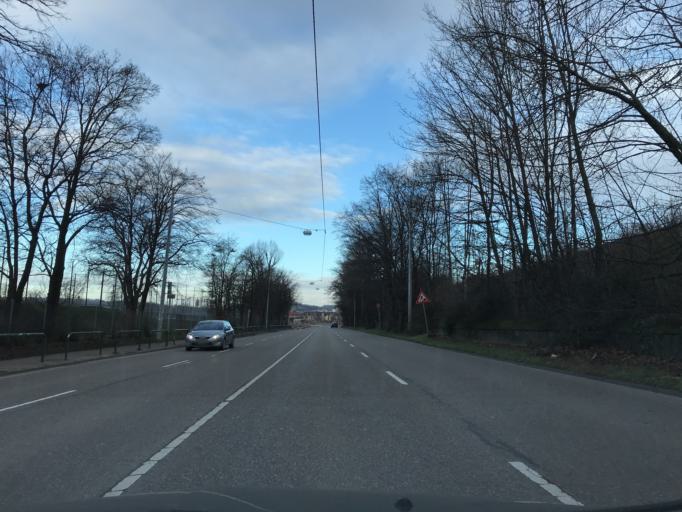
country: DE
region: Baden-Wuerttemberg
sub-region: Regierungsbezirk Stuttgart
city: Stuttgart-Ost
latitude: 48.7934
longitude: 9.2362
